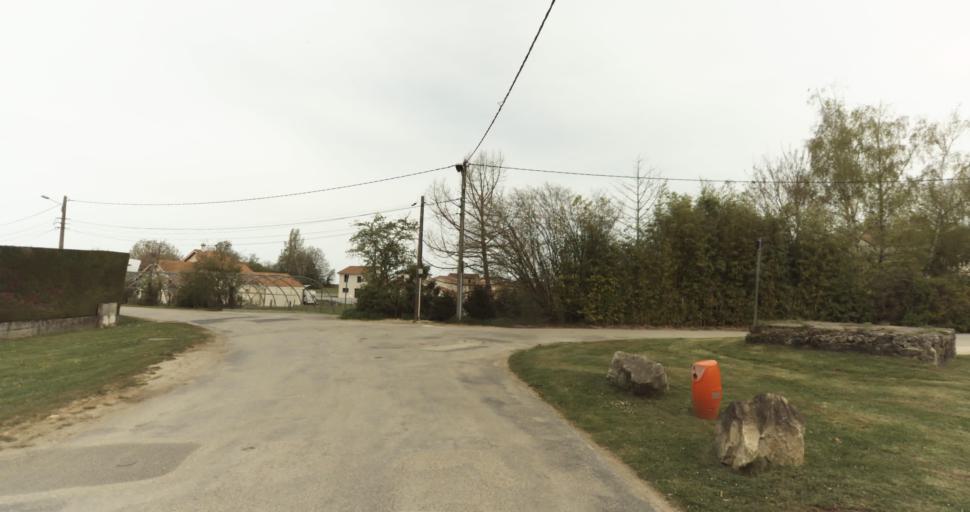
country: FR
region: Rhone-Alpes
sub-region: Departement de l'Ain
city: Amberieu-en-Bugey
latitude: 45.9640
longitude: 5.3667
